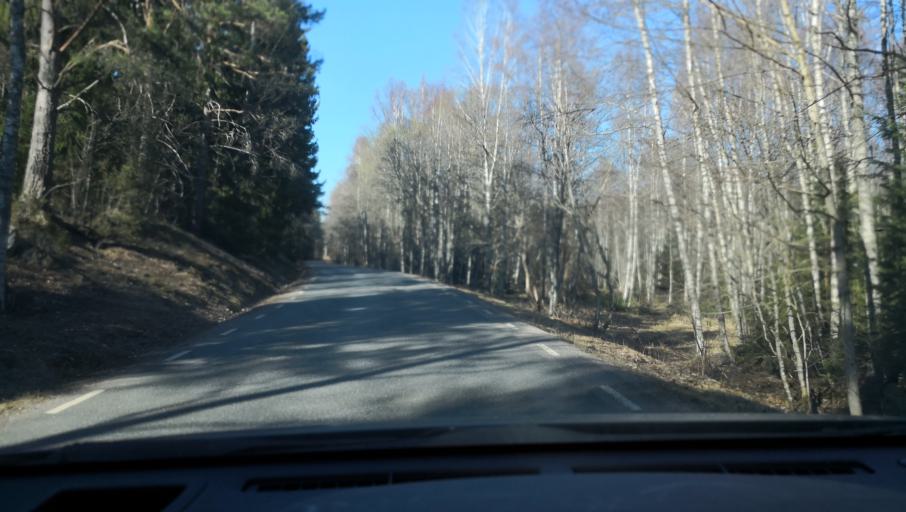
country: SE
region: Vaestmanland
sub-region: Sala Kommun
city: Sala
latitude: 59.9793
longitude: 16.4744
